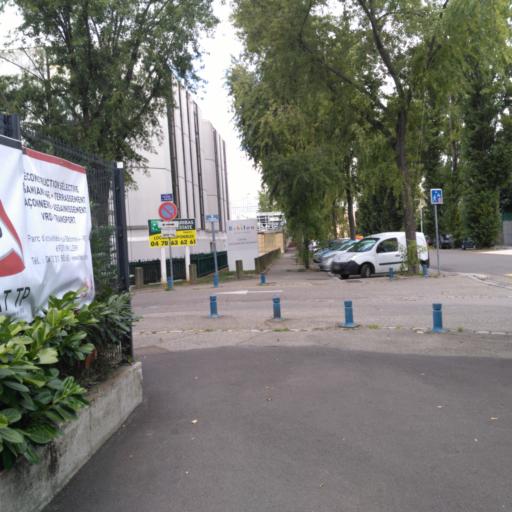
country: FR
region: Rhone-Alpes
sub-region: Departement du Rhone
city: La Mulatiere
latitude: 45.7274
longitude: 4.8270
